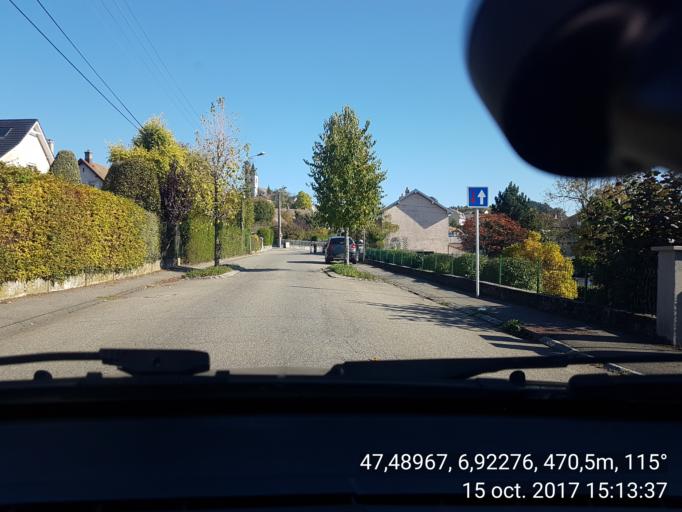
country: FR
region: Franche-Comte
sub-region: Territoire de Belfort
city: Beaucourt
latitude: 47.4896
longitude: 6.9227
